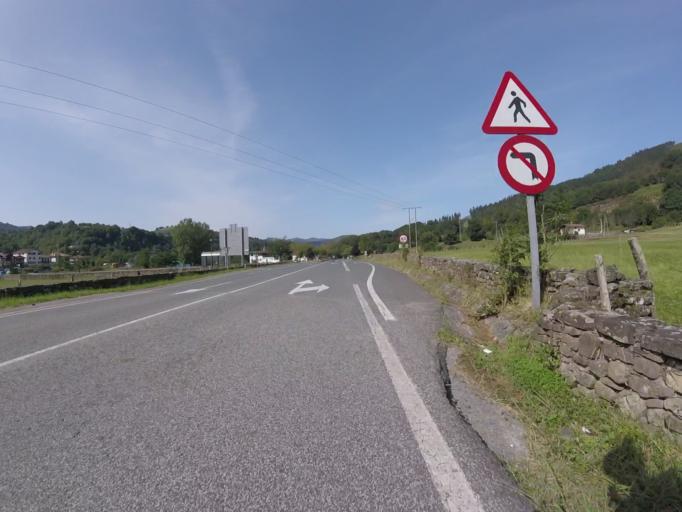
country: ES
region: Navarre
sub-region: Provincia de Navarra
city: Doneztebe
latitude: 43.1320
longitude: -1.6442
